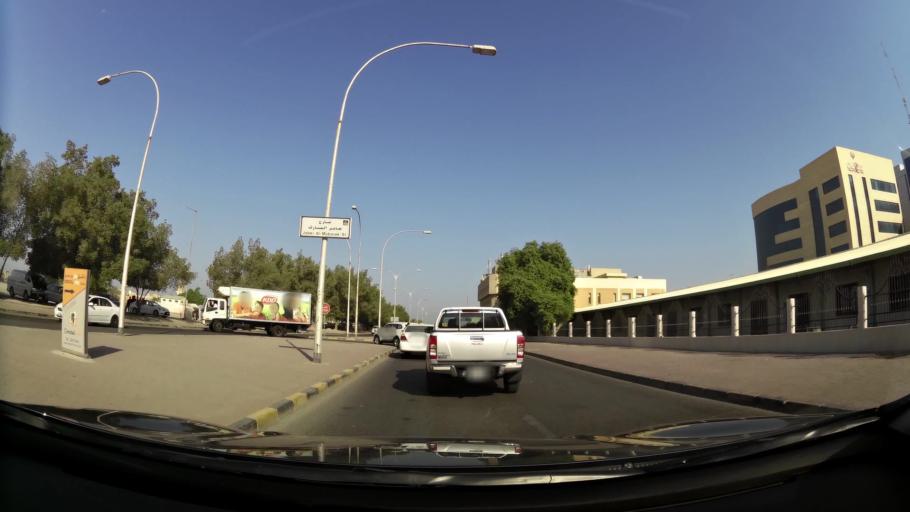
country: KW
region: Al Asimah
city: Kuwait City
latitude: 29.3868
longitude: 47.9866
